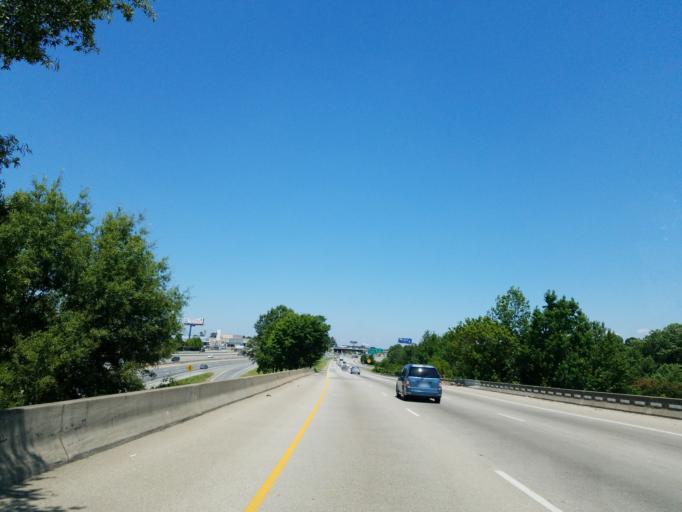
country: US
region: Georgia
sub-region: Fulton County
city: College Park
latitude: 33.6191
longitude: -84.4827
